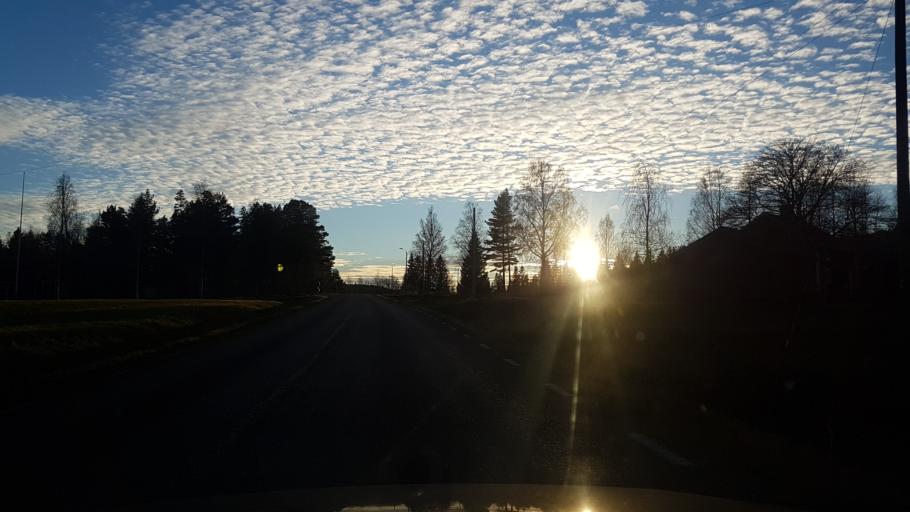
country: SE
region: Dalarna
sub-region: Leksand Municipality
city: Smedby
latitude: 60.7284
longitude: 15.1284
